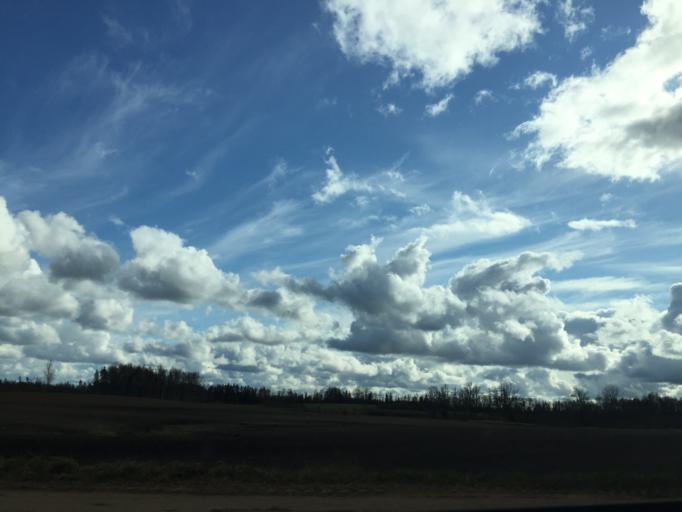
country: LV
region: Burtnieki
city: Matisi
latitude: 57.6190
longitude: 24.9933
